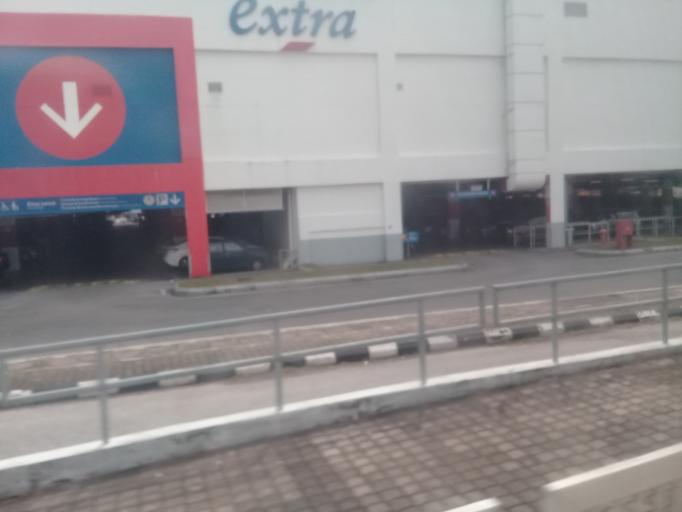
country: MY
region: Perak
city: Ipoh
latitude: 4.6159
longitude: 101.1183
